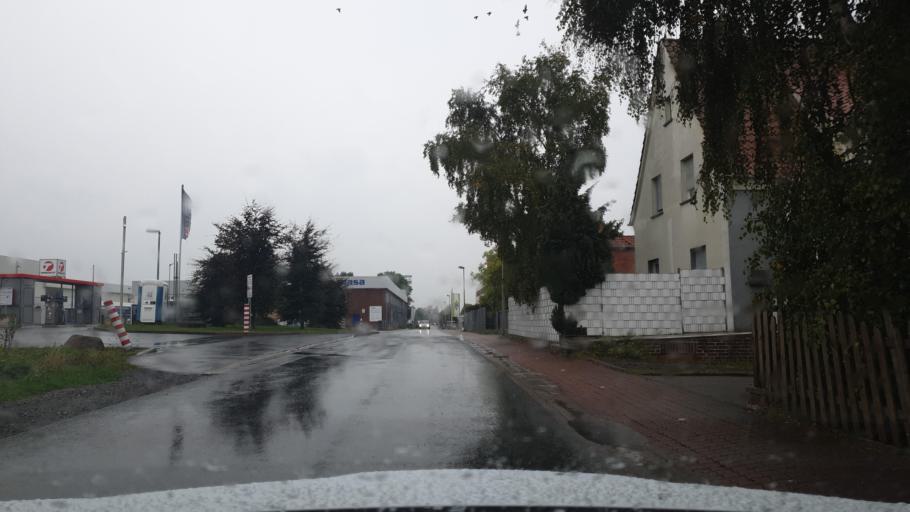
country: DE
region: North Rhine-Westphalia
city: Porta Westfalica
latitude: 52.2081
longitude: 8.8825
